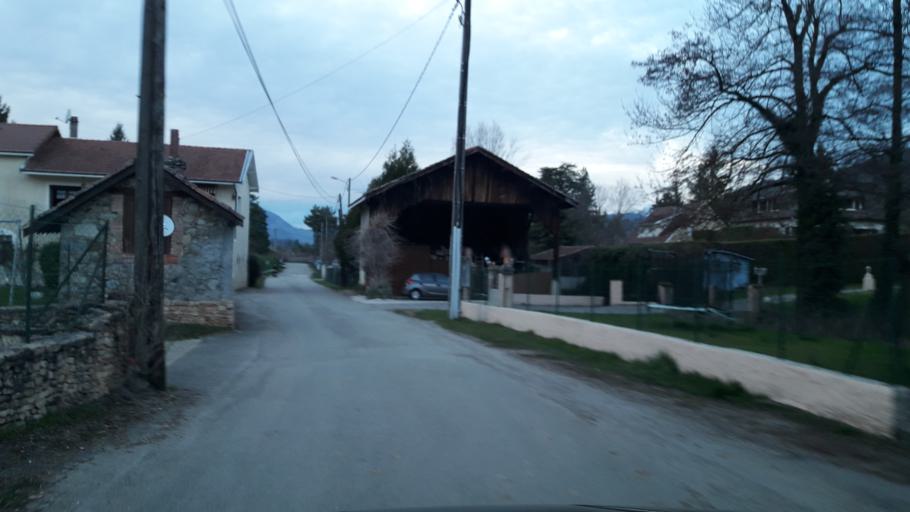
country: FR
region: Rhone-Alpes
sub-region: Departement de l'Isere
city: Brie-et-Angonnes
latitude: 45.1272
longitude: 5.7862
